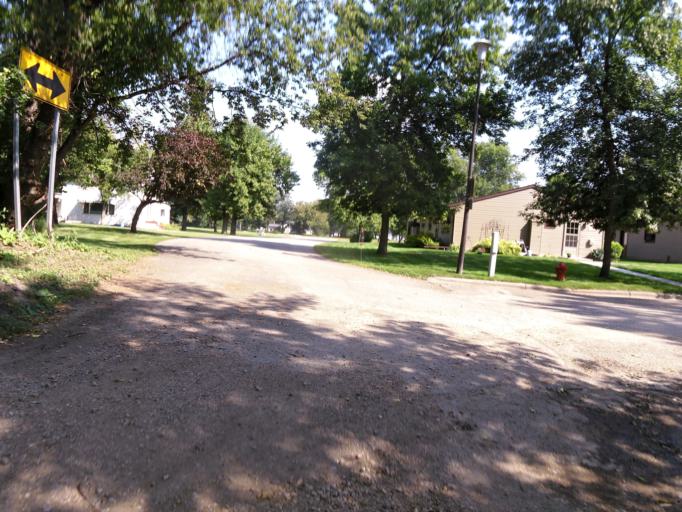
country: US
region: North Dakota
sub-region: Walsh County
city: Grafton
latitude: 48.4234
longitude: -97.3998
